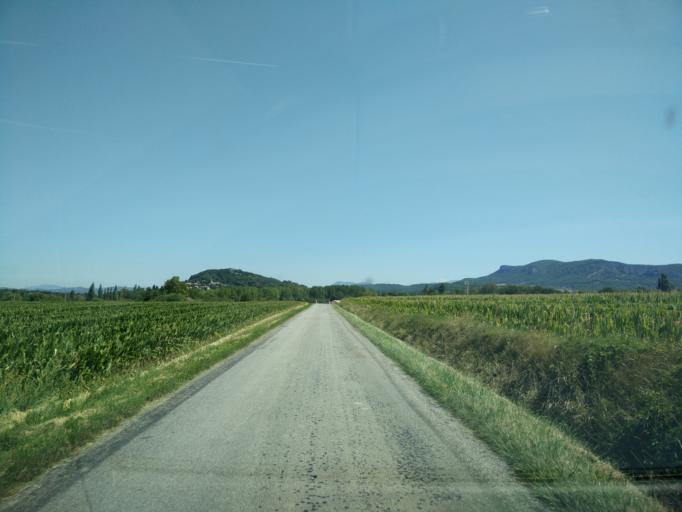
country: FR
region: Rhone-Alpes
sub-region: Departement de la Drome
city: La Begude-de-Mazenc
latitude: 44.5348
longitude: 4.9225
